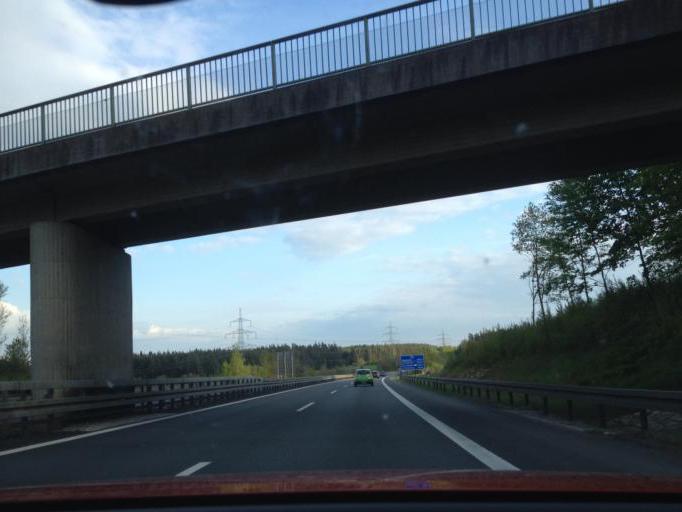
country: DE
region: Bavaria
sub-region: Upper Palatinate
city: Wiesau
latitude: 49.9067
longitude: 12.2209
